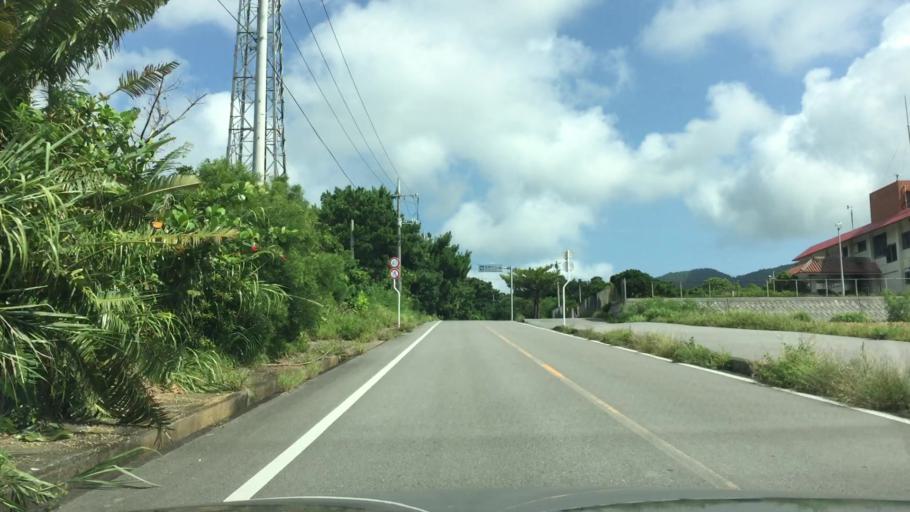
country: JP
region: Okinawa
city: Ishigaki
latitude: 24.4198
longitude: 124.2145
